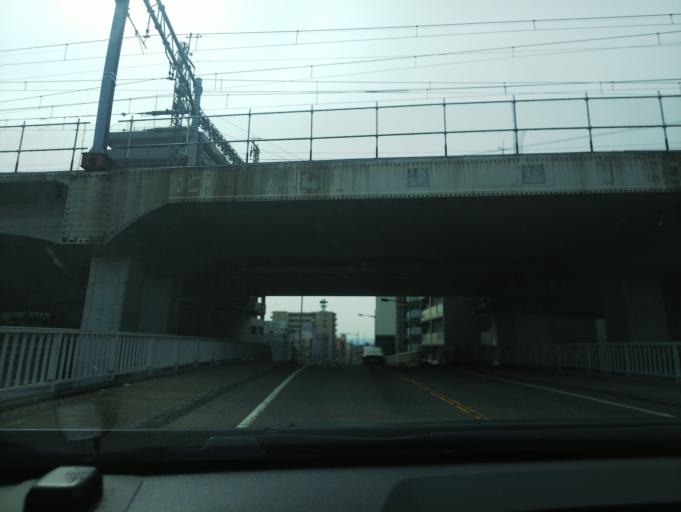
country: JP
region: Niigata
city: Niigata-shi
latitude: 37.9135
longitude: 139.0668
